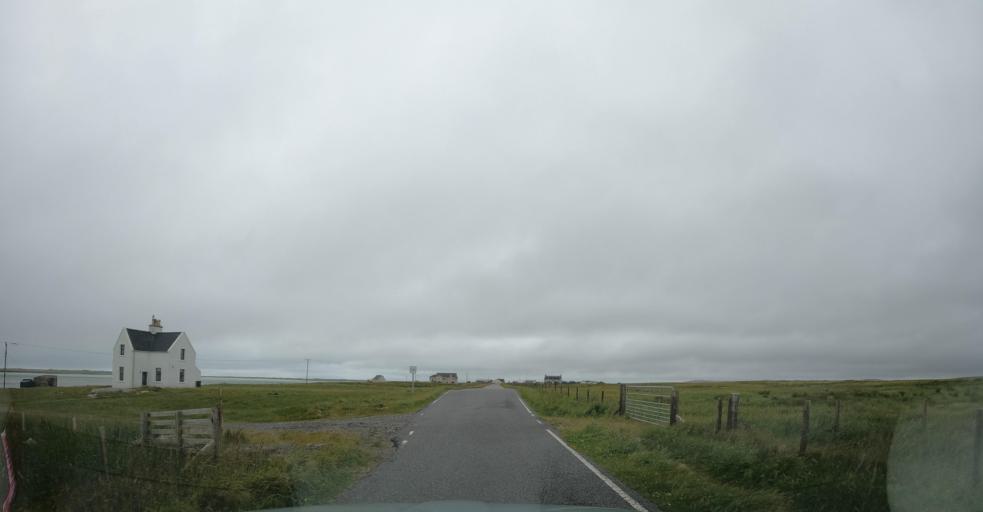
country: GB
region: Scotland
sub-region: Eilean Siar
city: Isle of North Uist
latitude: 57.5583
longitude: -7.3651
